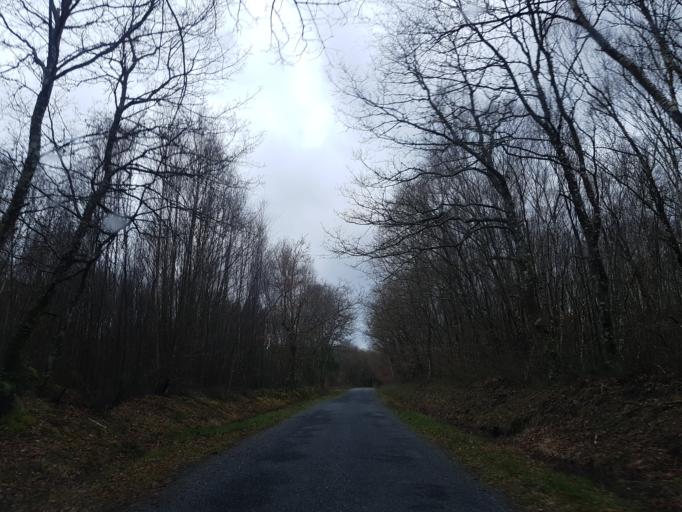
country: ES
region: Galicia
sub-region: Provincia de Lugo
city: Friol
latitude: 43.1206
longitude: -7.8210
